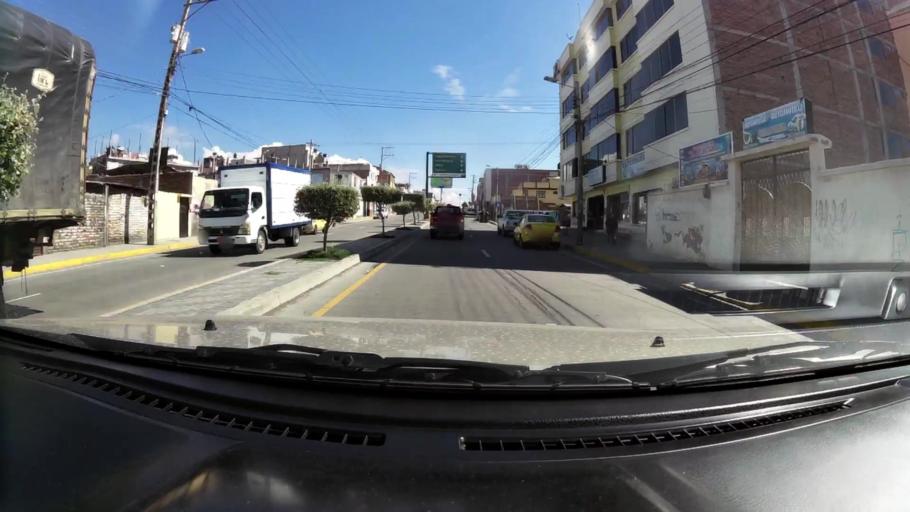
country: EC
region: Chimborazo
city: Riobamba
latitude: -1.6623
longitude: -78.6490
